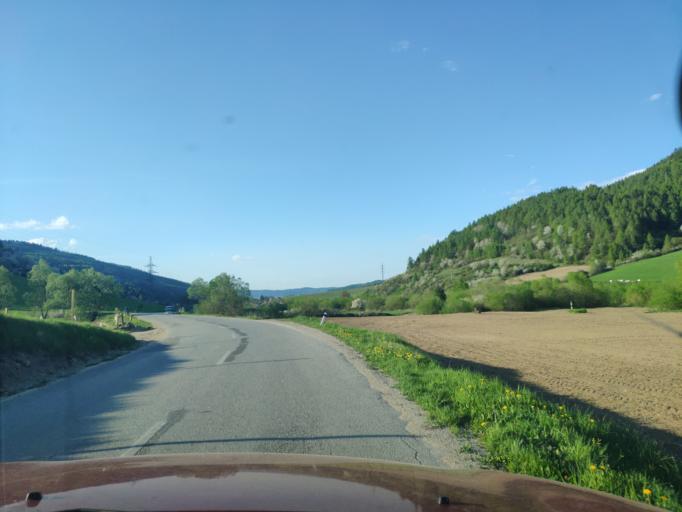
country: SK
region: Presovsky
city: Spisske Podhradie
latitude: 49.0871
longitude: 20.8479
